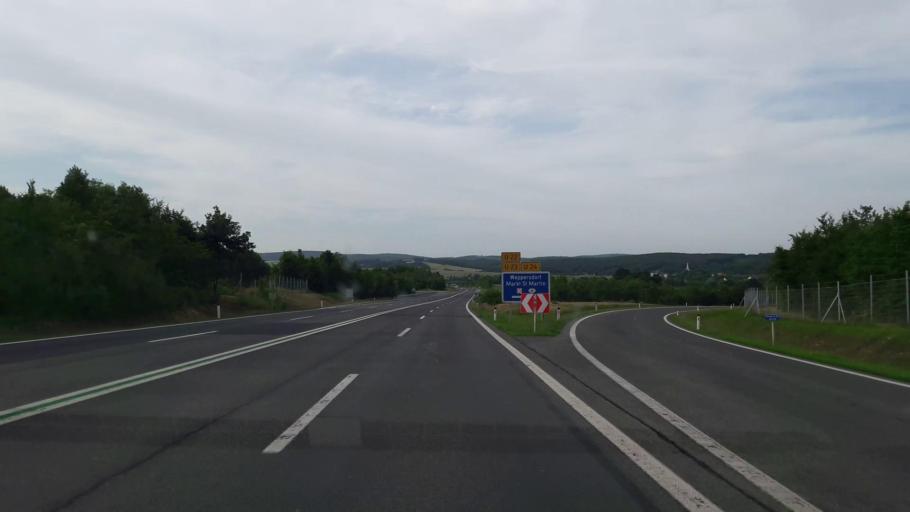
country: AT
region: Burgenland
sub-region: Politischer Bezirk Oberpullendorf
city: Markt Sankt Martin
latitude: 47.5695
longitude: 16.4155
